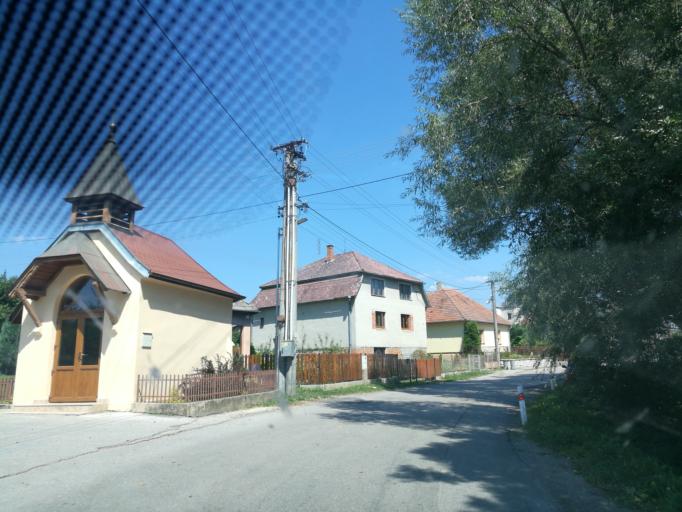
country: SK
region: Nitriansky
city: Banovce nad Bebravou
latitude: 48.7368
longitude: 18.1664
